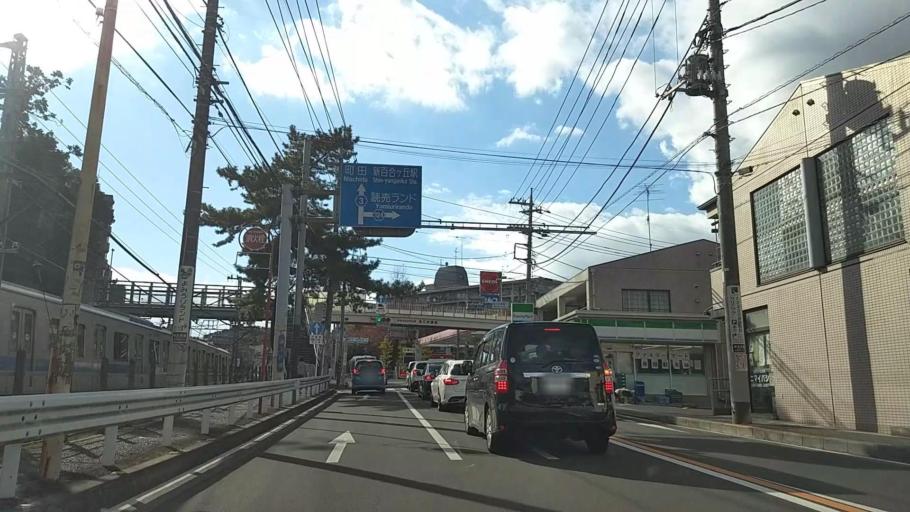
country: JP
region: Tokyo
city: Chofugaoka
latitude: 35.6146
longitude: 139.5240
